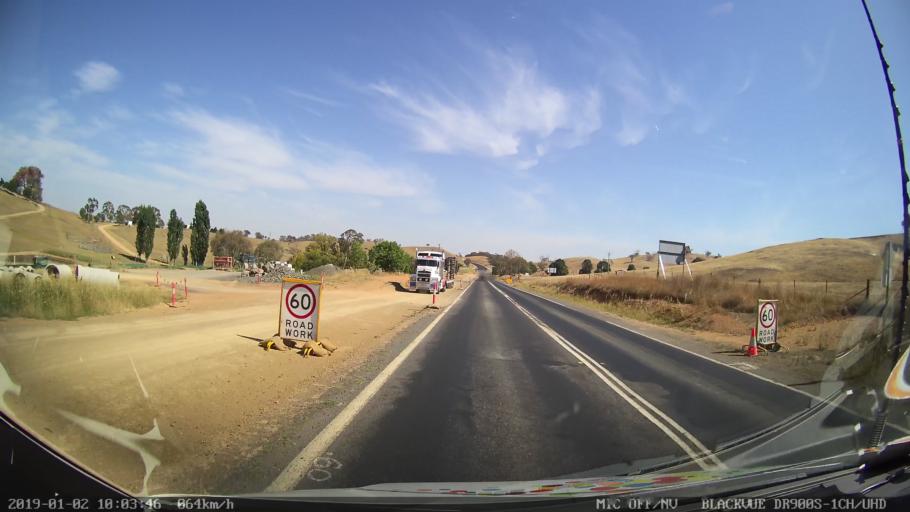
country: AU
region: New South Wales
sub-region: Gundagai
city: Gundagai
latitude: -35.1745
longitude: 148.1253
